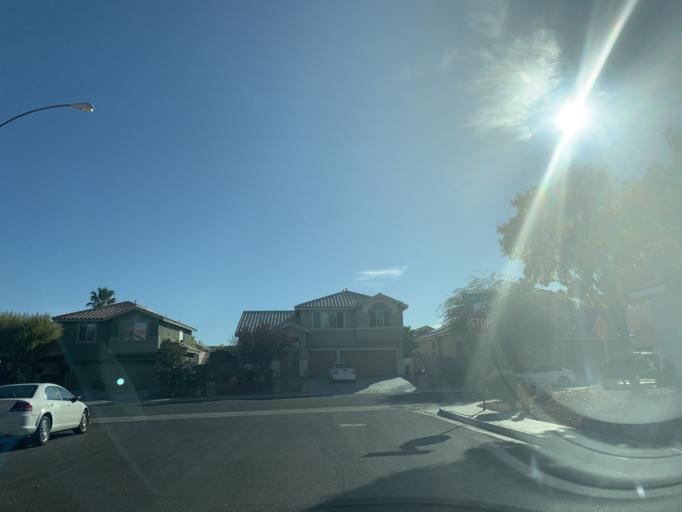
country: US
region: Nevada
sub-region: Clark County
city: Summerlin South
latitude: 36.1275
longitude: -115.3086
